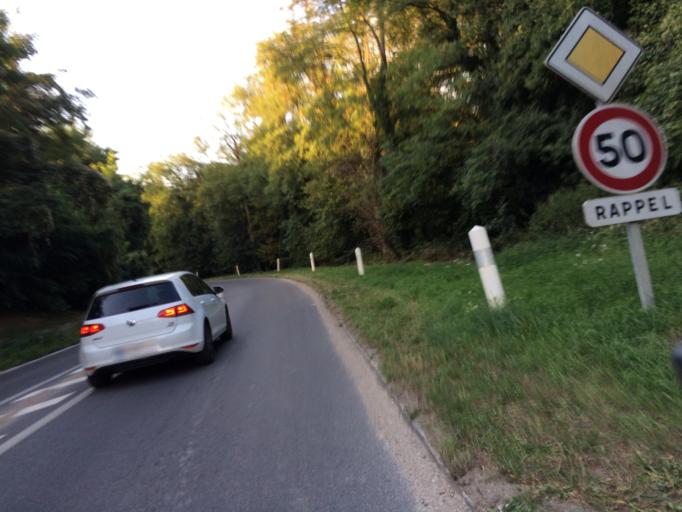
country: FR
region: Ile-de-France
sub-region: Departement de l'Essonne
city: Nozay
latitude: 48.6620
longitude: 2.2053
